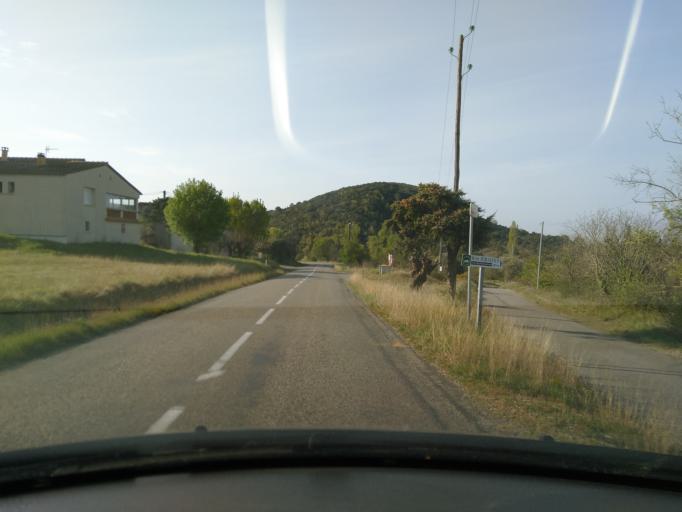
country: FR
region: Rhone-Alpes
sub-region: Departement de l'Ardeche
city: Ruoms
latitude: 44.4353
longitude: 4.4106
